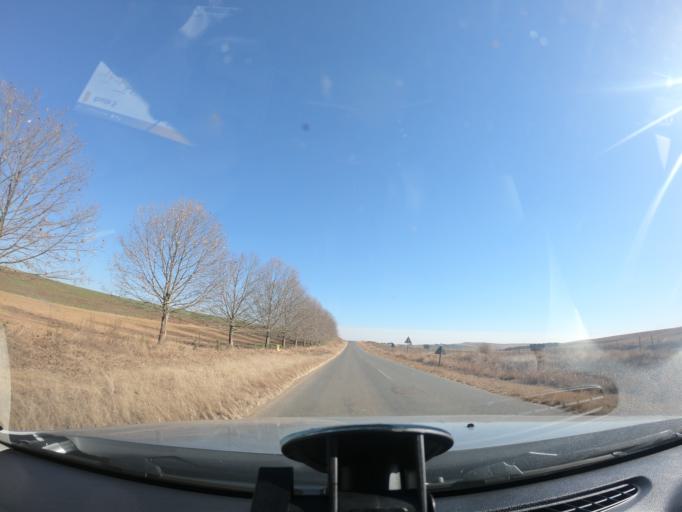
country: ZA
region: KwaZulu-Natal
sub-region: uMgungundlovu District Municipality
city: Mooirivier
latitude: -29.3273
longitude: 29.8409
